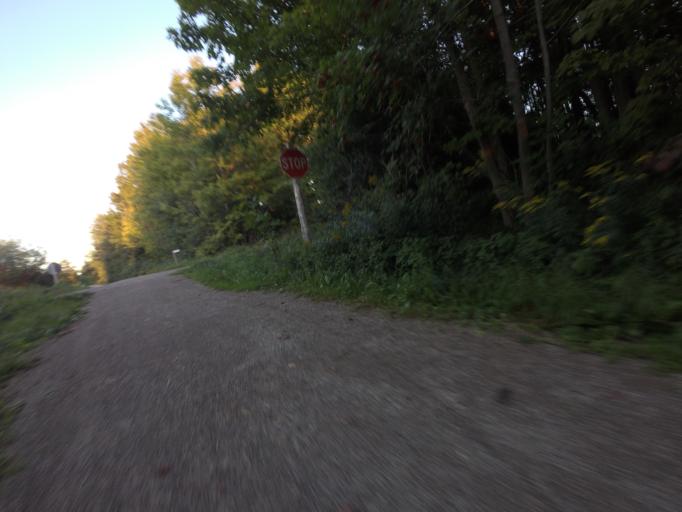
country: CA
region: Ontario
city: Goderich
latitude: 43.7481
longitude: -81.6335
